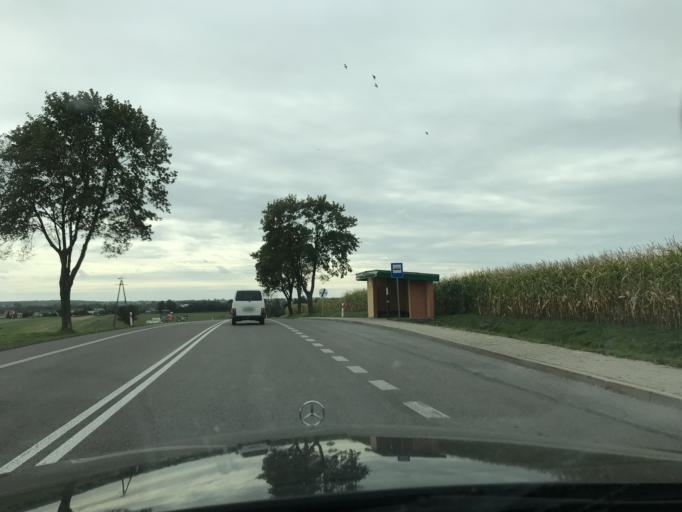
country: PL
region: Lublin Voivodeship
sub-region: Powiat lubelski
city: Niedrzwica Duza
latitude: 51.1428
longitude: 22.3970
